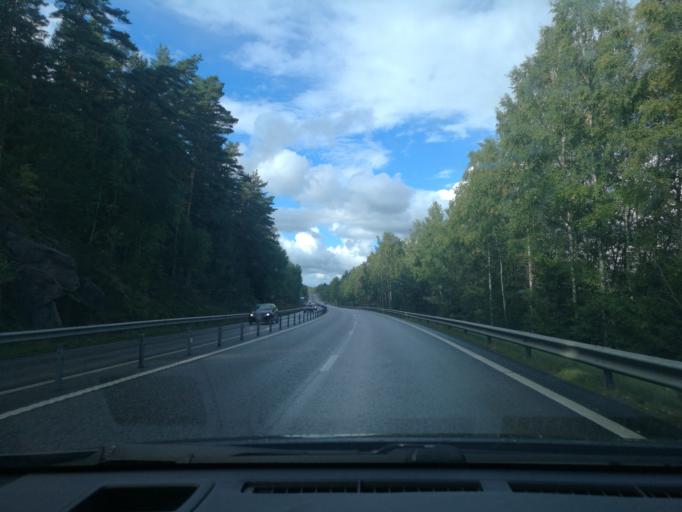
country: SE
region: OEstergoetland
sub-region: Norrkopings Kommun
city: Jursla
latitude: 58.7517
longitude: 16.1765
